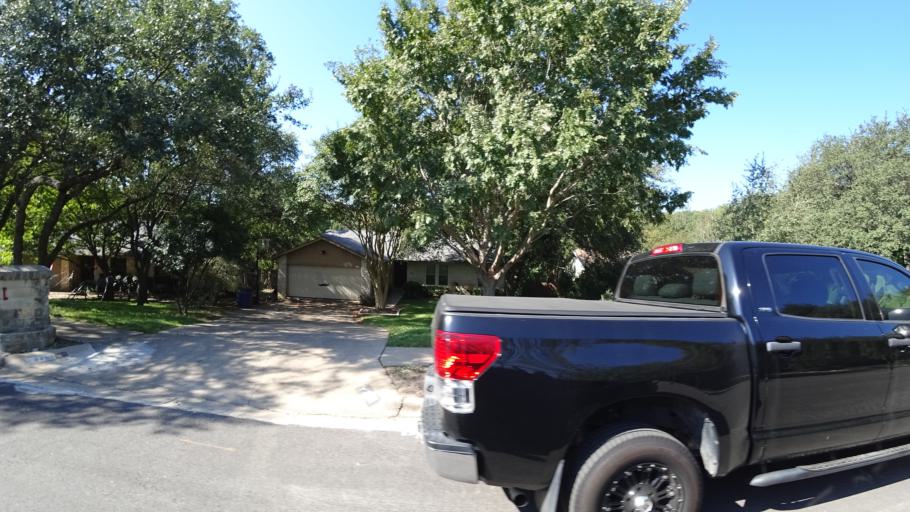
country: US
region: Texas
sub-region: Travis County
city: Rollingwood
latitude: 30.2727
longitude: -97.8052
